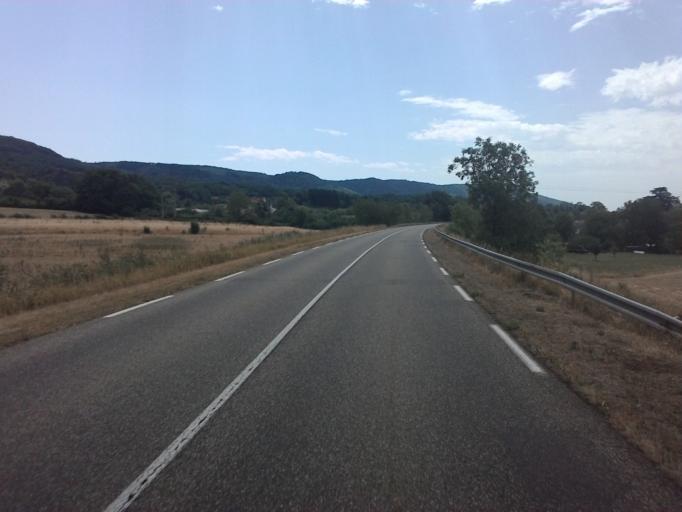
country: FR
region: Franche-Comte
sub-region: Departement du Jura
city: Saint-Amour
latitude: 46.4375
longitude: 5.3533
